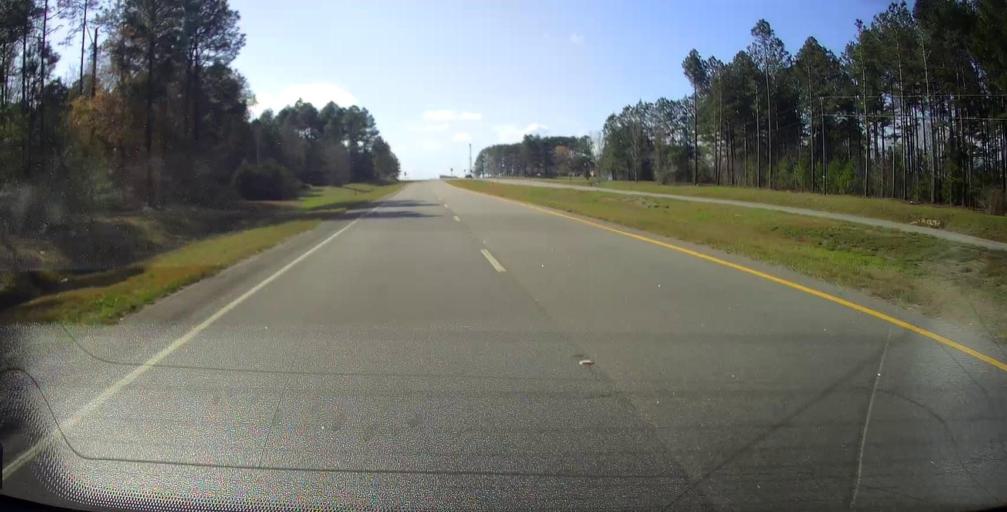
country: US
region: Georgia
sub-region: Dodge County
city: Eastman
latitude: 32.2018
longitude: -83.2596
